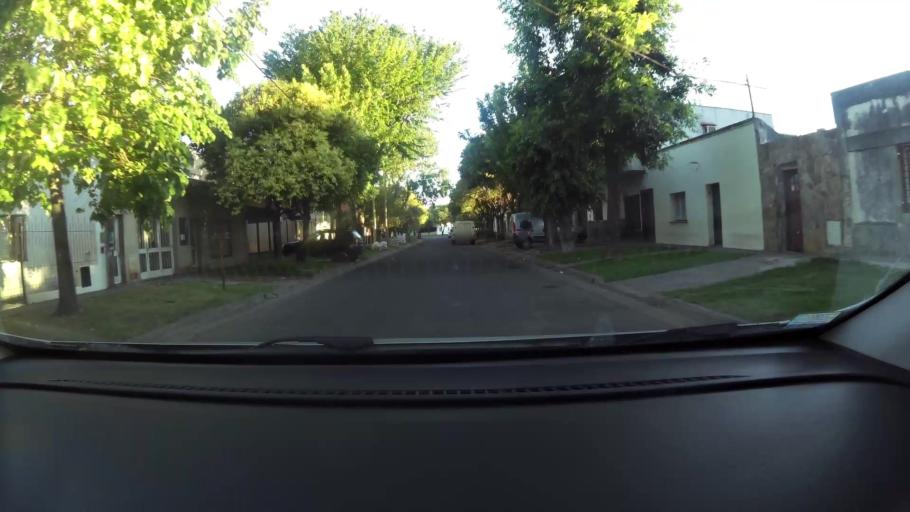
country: AR
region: Santa Fe
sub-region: Departamento de Rosario
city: Rosario
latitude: -32.9713
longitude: -60.6714
